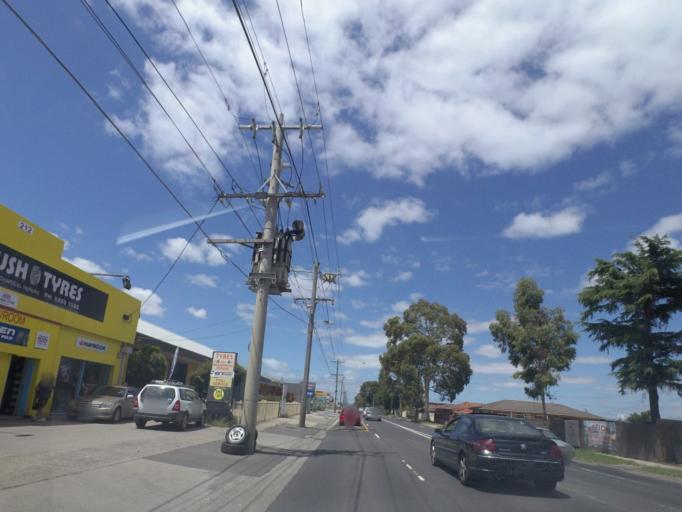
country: AU
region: Victoria
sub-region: Brimbank
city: Albion
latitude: -37.7552
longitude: 144.8328
